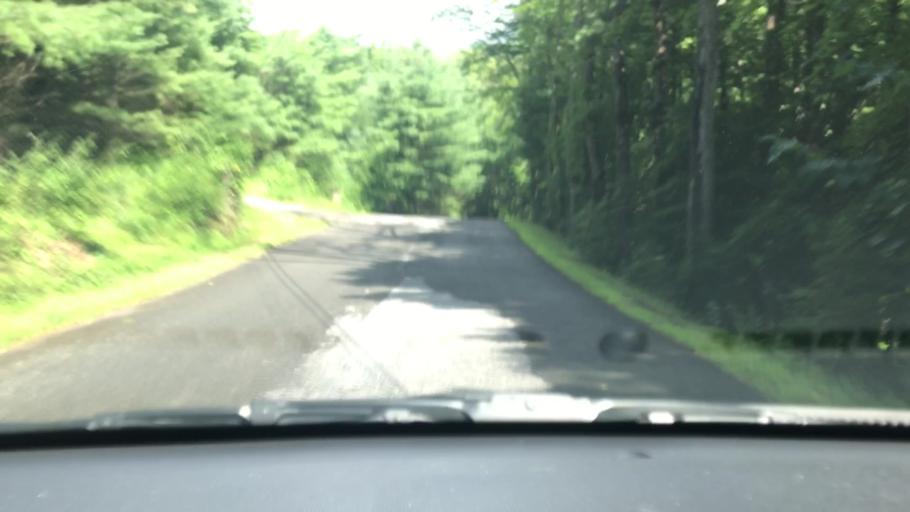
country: US
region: New York
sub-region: Ulster County
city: Shokan
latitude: 41.9623
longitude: -74.2827
